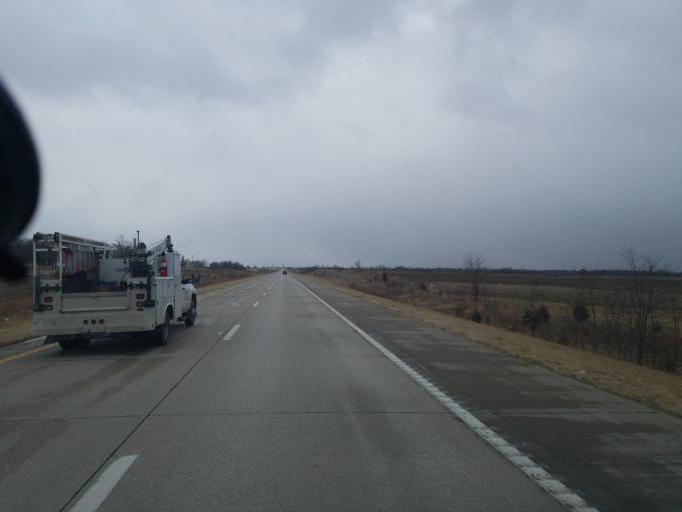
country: US
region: Missouri
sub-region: Randolph County
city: Moberly
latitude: 39.4800
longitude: -92.4347
